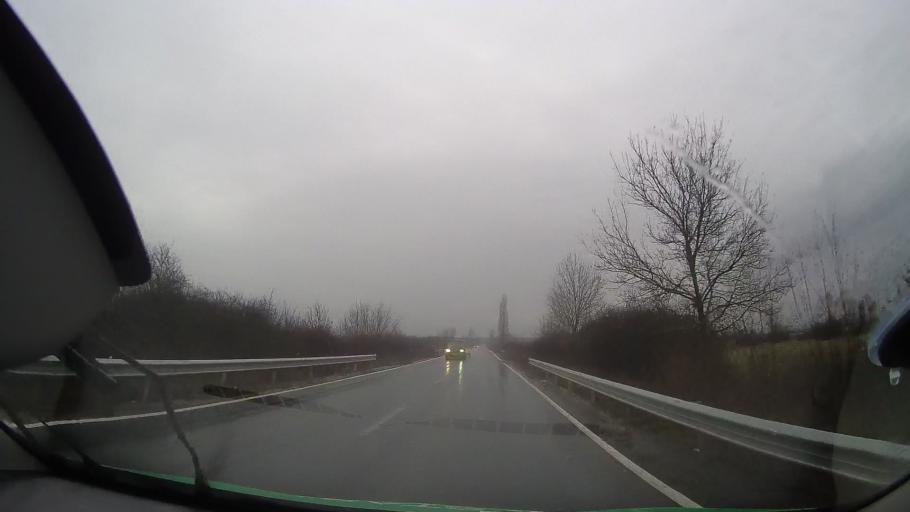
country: RO
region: Bihor
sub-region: Comuna Tinca
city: Tinca
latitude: 46.7450
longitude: 21.9390
